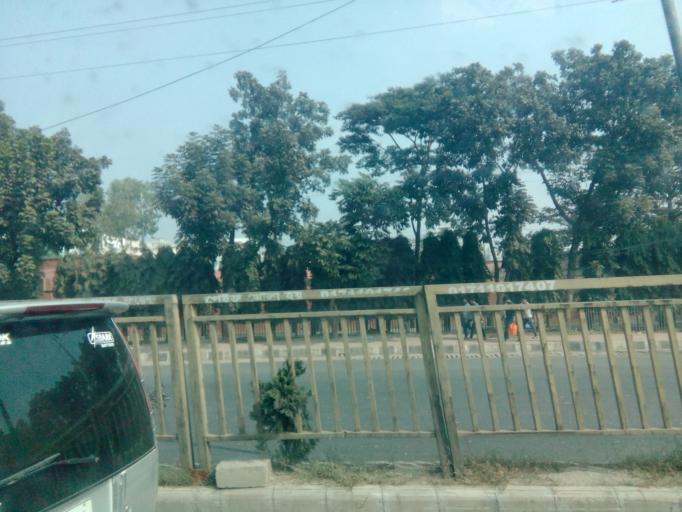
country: BD
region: Dhaka
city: Paltan
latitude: 23.7961
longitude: 90.4240
